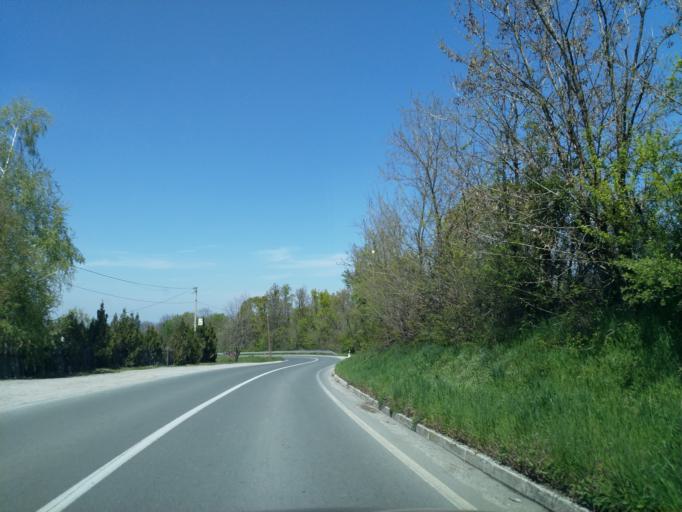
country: RS
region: Central Serbia
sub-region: Belgrade
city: Lazarevac
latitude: 44.3705
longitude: 20.3212
